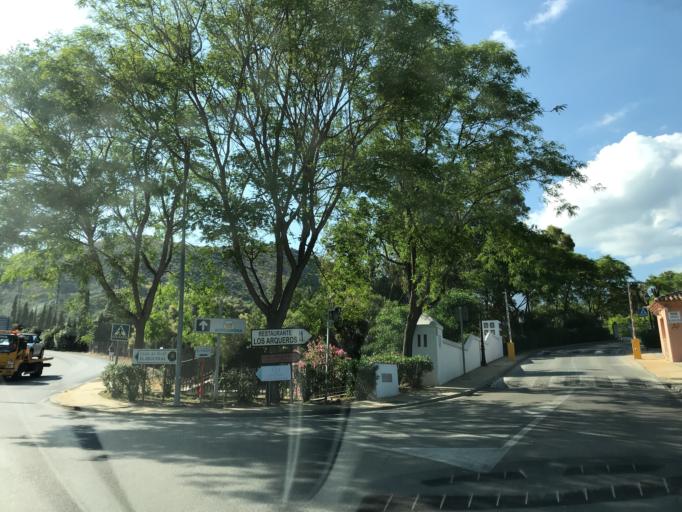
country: ES
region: Andalusia
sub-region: Provincia de Malaga
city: Benahavis
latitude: 36.5072
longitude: -5.0156
